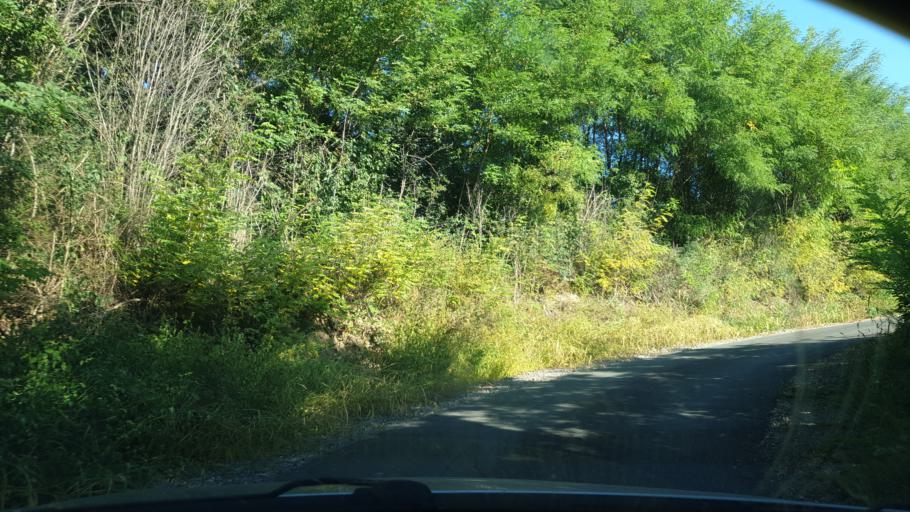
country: RS
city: Jarebice
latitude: 44.5014
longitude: 19.4885
